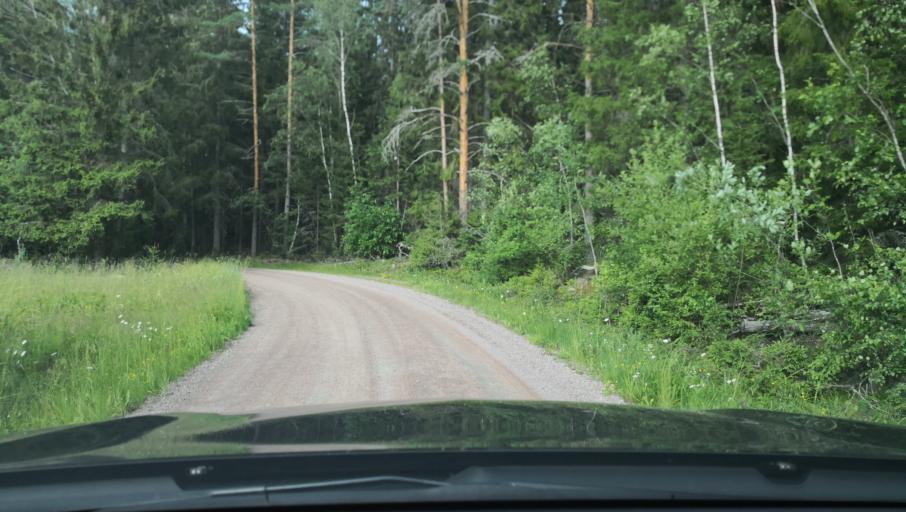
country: SE
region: Vaestmanland
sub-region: Surahammars Kommun
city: Surahammar
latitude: 59.6591
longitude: 16.1543
